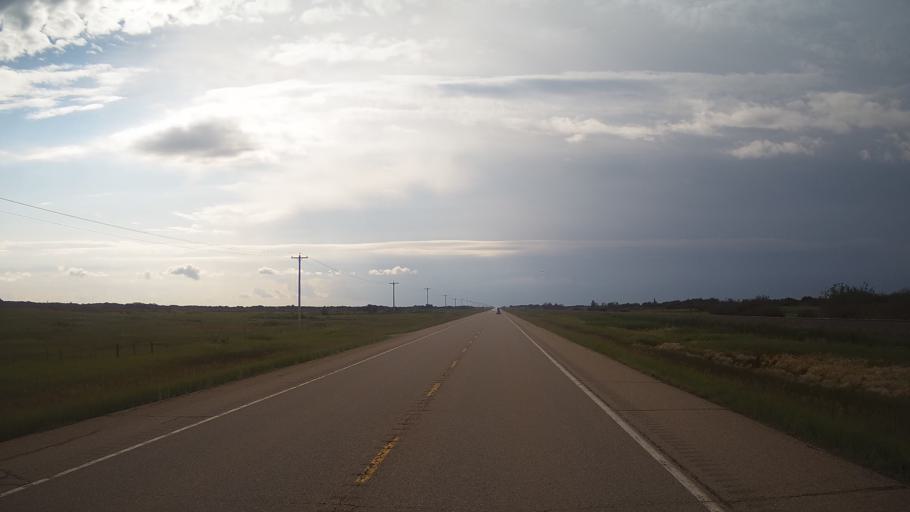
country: CA
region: Alberta
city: Viking
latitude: 53.1397
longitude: -111.9349
